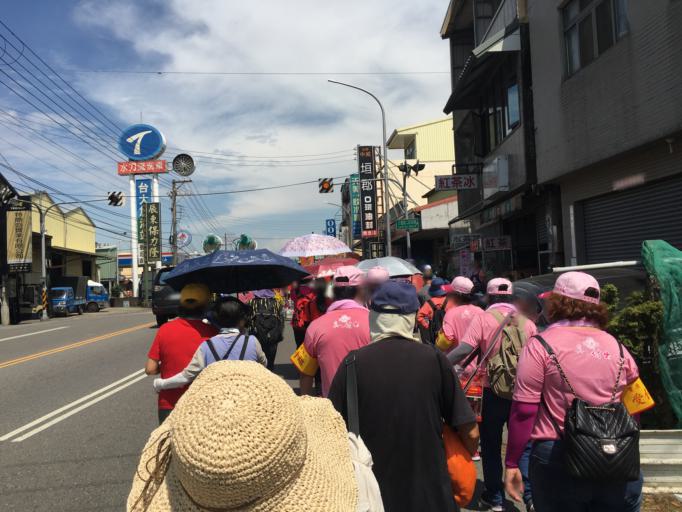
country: TW
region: Taiwan
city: Fengyuan
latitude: 24.2715
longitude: 120.7218
